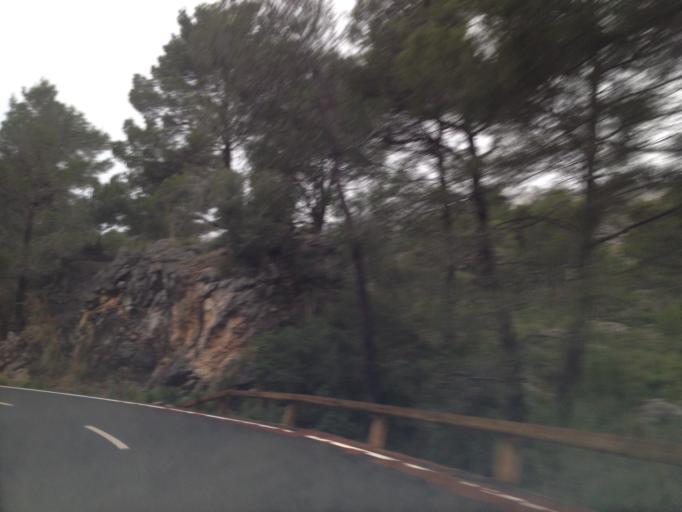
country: ES
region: Balearic Islands
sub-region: Illes Balears
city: Fornalutx
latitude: 39.7952
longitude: 2.7477
